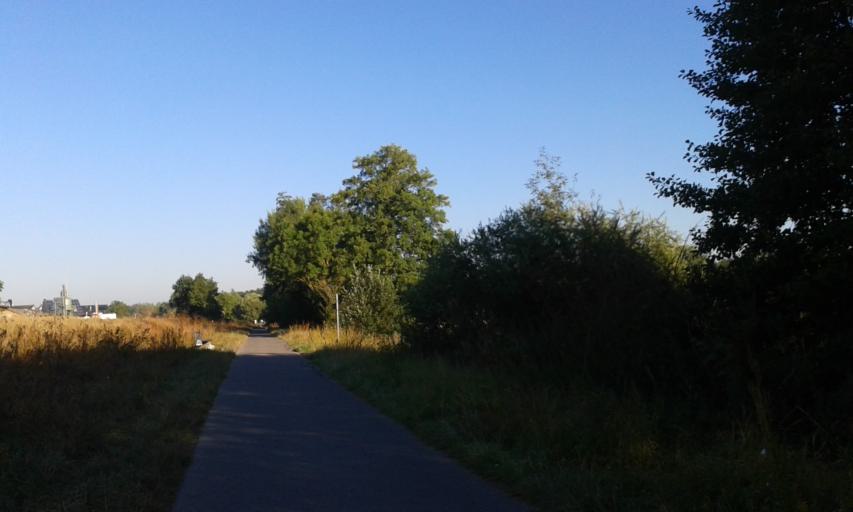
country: DE
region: Bavaria
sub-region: Upper Franconia
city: Bischberg
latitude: 49.9108
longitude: 10.8368
